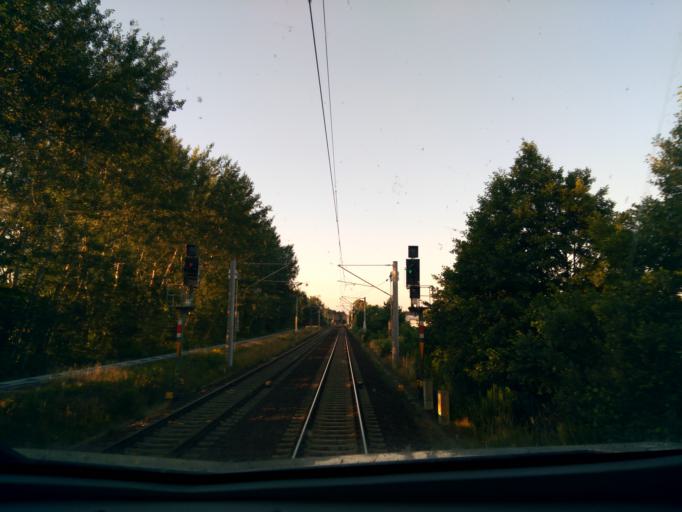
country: DE
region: Brandenburg
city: Bestensee
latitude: 52.2464
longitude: 13.6337
